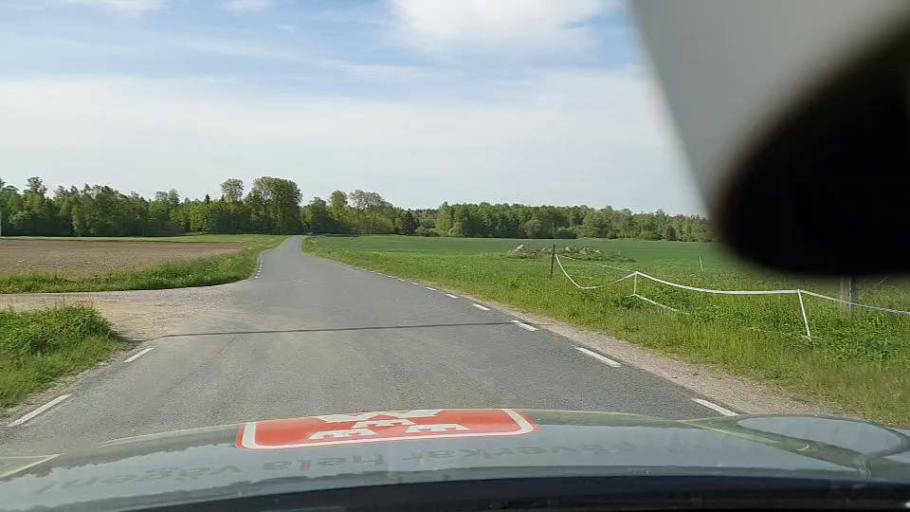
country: SE
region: Soedermanland
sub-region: Eskilstuna Kommun
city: Arla
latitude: 59.2701
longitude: 16.6612
